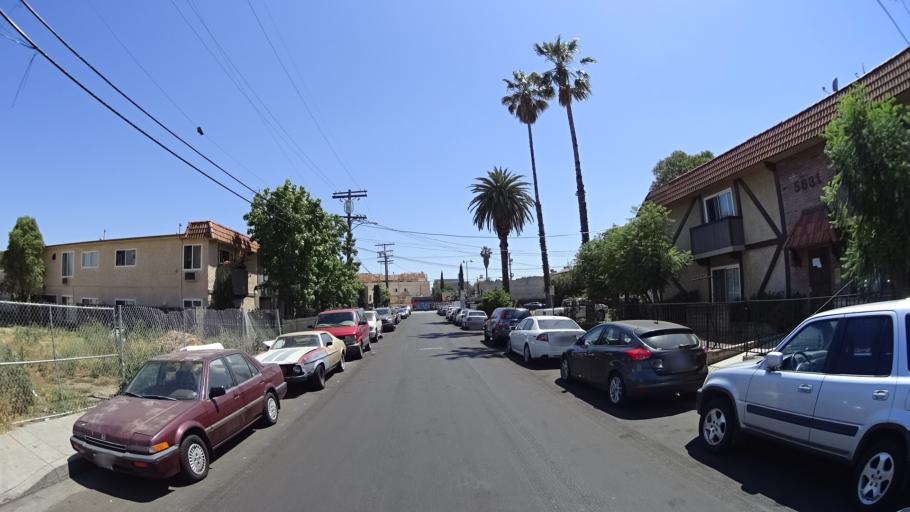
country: US
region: California
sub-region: Los Angeles County
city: North Hollywood
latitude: 34.1731
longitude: -118.3747
